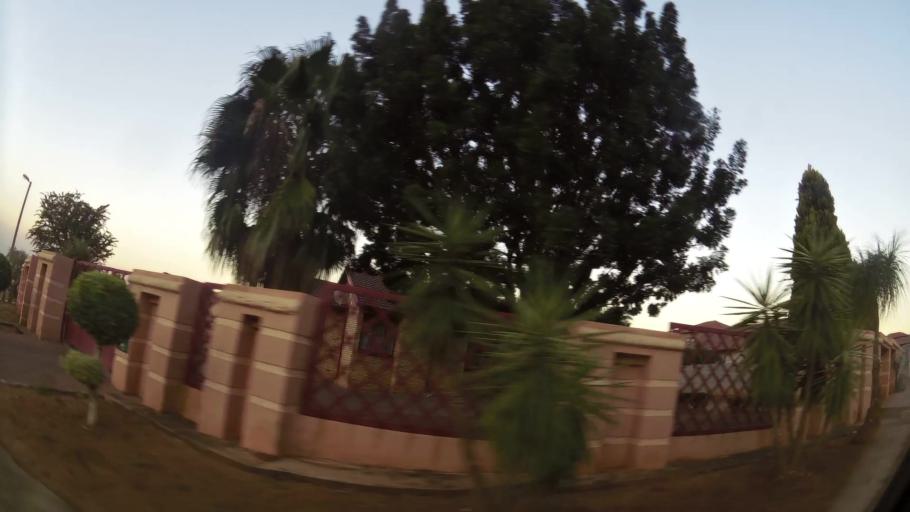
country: ZA
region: North-West
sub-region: Bojanala Platinum District Municipality
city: Rustenburg
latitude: -25.6525
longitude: 27.2010
